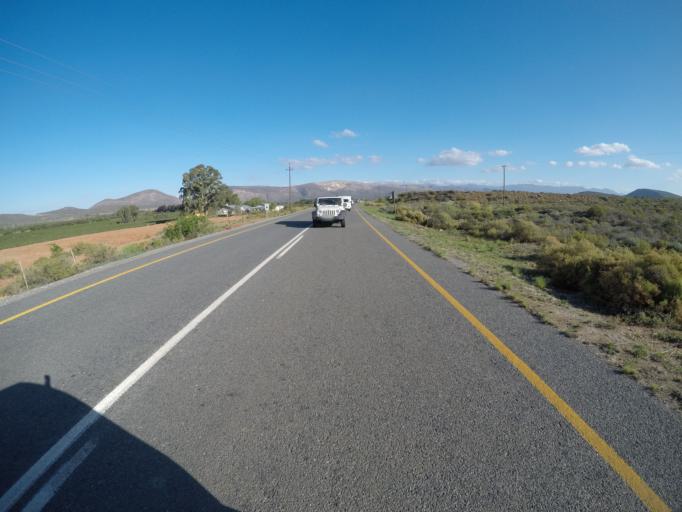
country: ZA
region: Western Cape
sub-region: Cape Winelands District Municipality
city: Ashton
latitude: -33.7937
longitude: 19.7803
